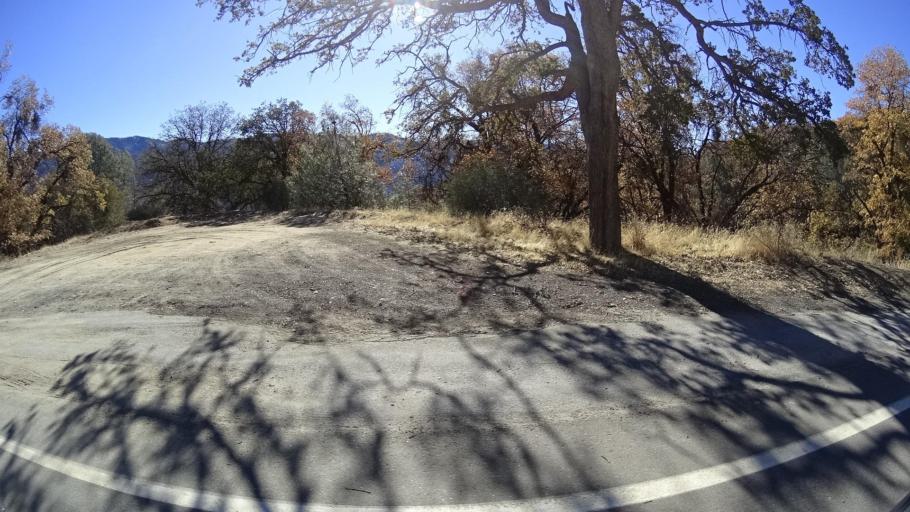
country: US
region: California
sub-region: Kern County
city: Alta Sierra
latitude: 35.7407
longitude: -118.6084
